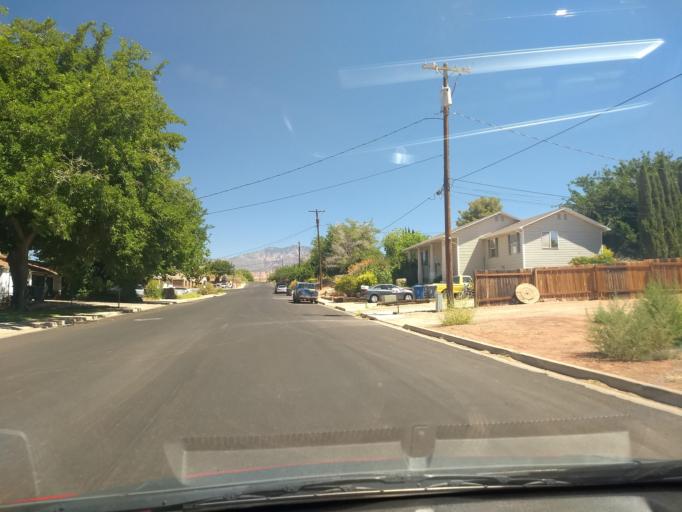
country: US
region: Utah
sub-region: Washington County
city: Washington
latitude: 37.1346
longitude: -113.5065
